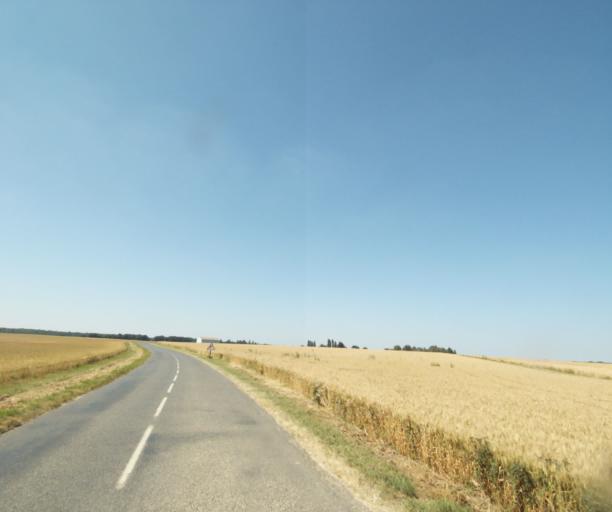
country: FR
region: Ile-de-France
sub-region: Departement de Seine-et-Marne
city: La Chapelle-la-Reine
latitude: 48.3356
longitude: 2.5623
